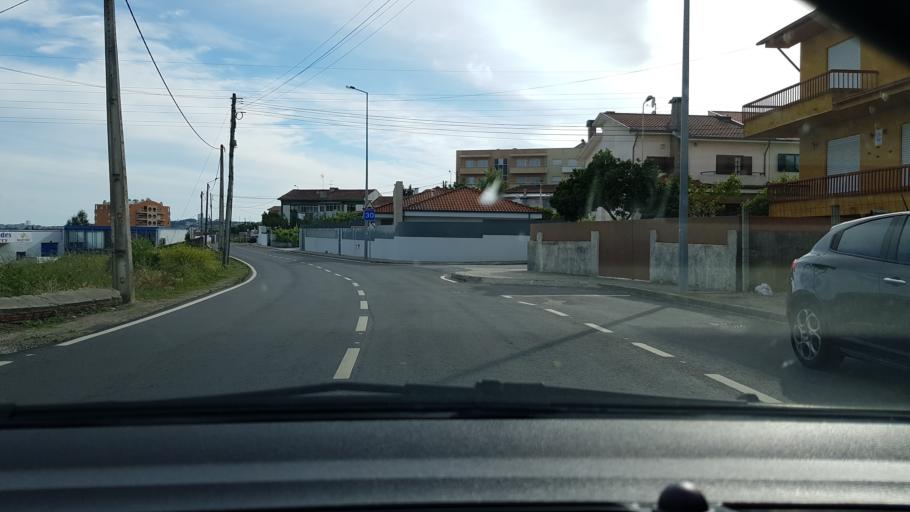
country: PT
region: Porto
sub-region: Gondomar
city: Baguim do Monte
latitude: 41.1925
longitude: -8.5499
